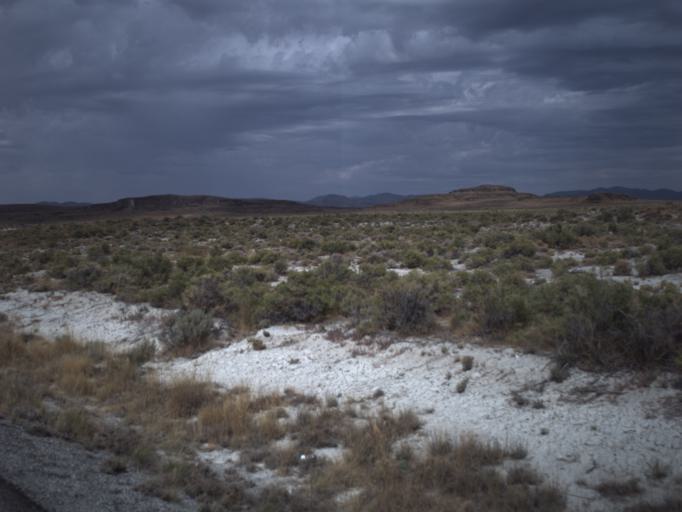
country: US
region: Utah
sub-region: Tooele County
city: Wendover
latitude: 41.4243
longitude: -113.8627
